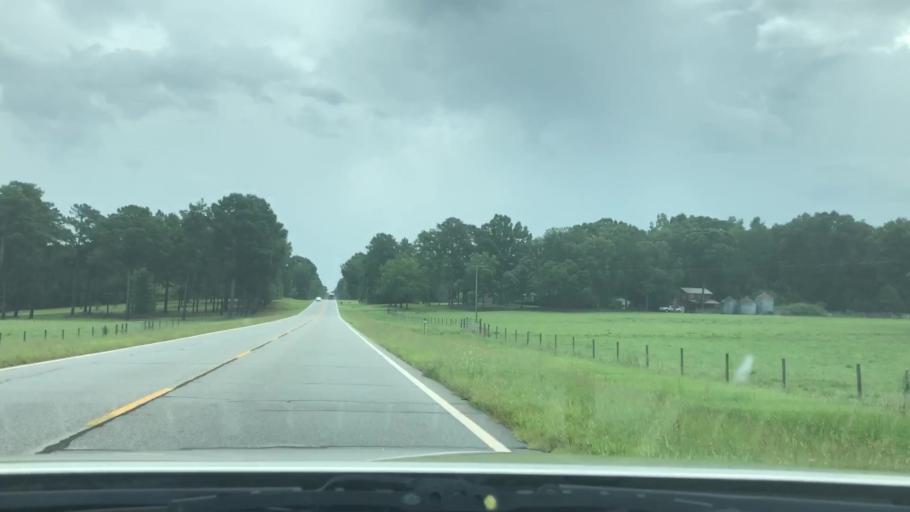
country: US
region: Georgia
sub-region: Pike County
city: Zebulon
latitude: 33.0928
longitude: -84.2802
